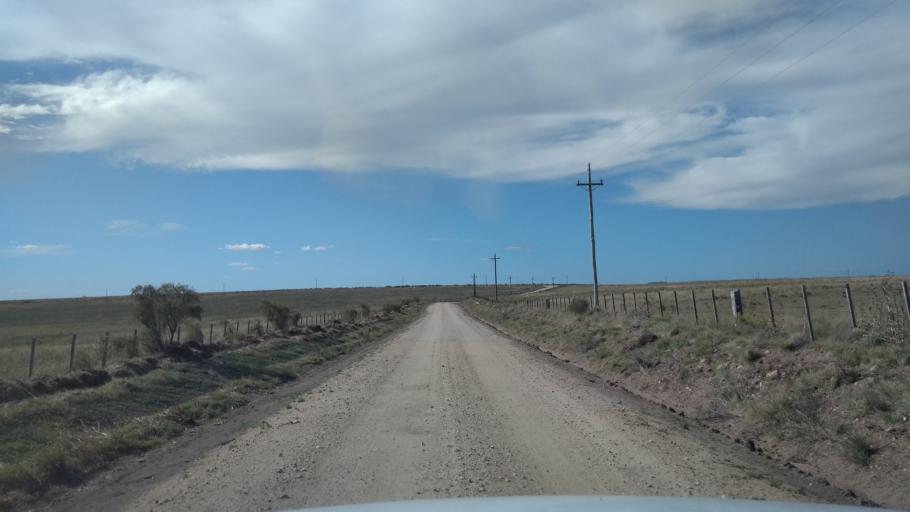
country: UY
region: Florida
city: Casupa
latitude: -34.0057
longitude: -55.7875
